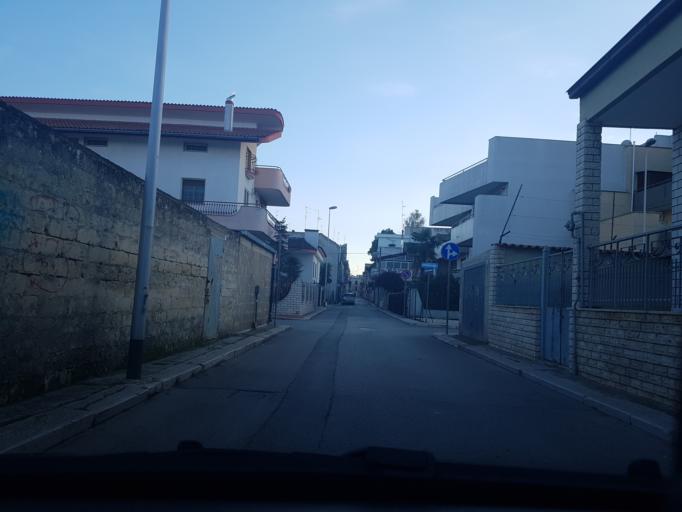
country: IT
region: Apulia
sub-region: Provincia di Bari
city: Bitritto
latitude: 41.0442
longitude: 16.8253
